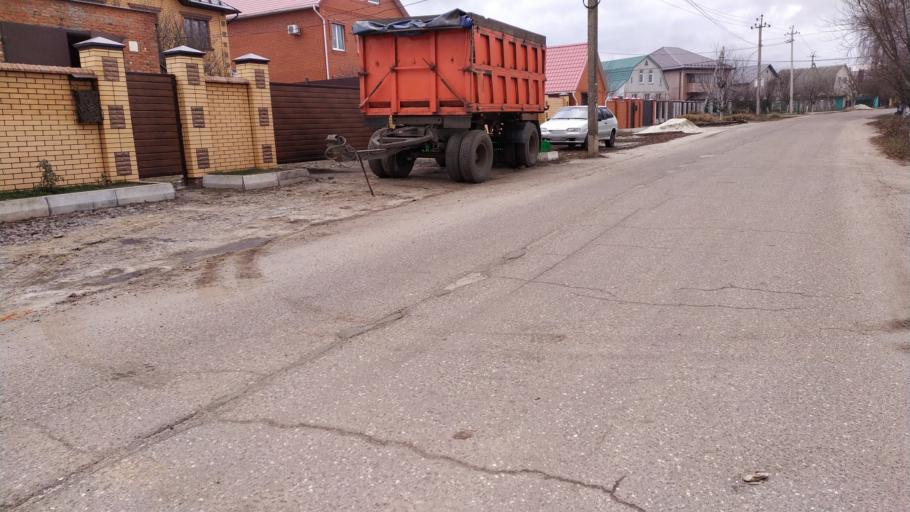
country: RU
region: Kursk
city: Kursk
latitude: 51.6382
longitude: 36.1419
